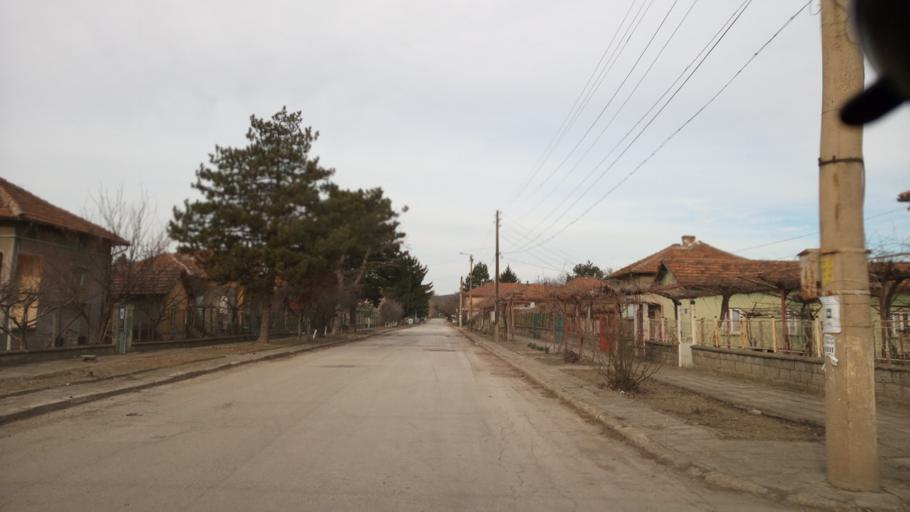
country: BG
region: Pleven
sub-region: Obshtina Belene
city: Belene
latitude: 43.6282
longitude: 25.0448
